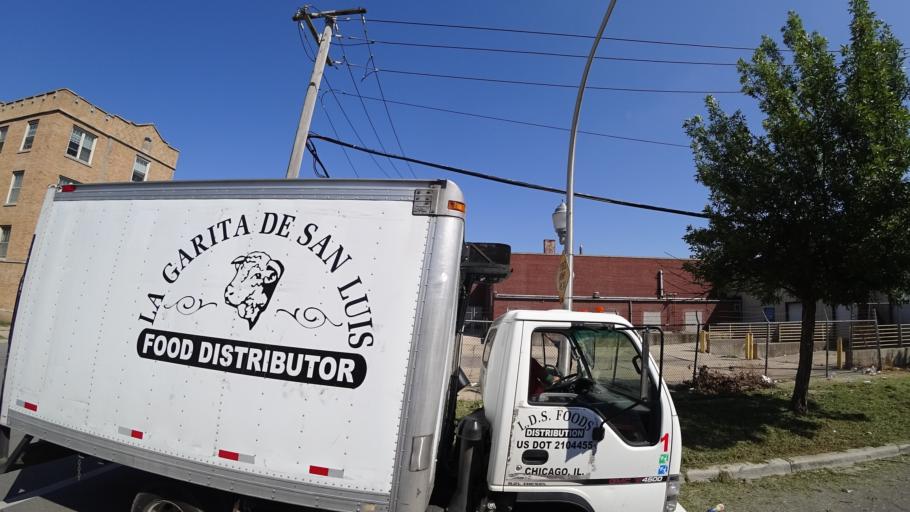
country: US
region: Illinois
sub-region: Cook County
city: Cicero
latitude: 41.8726
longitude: -87.7180
